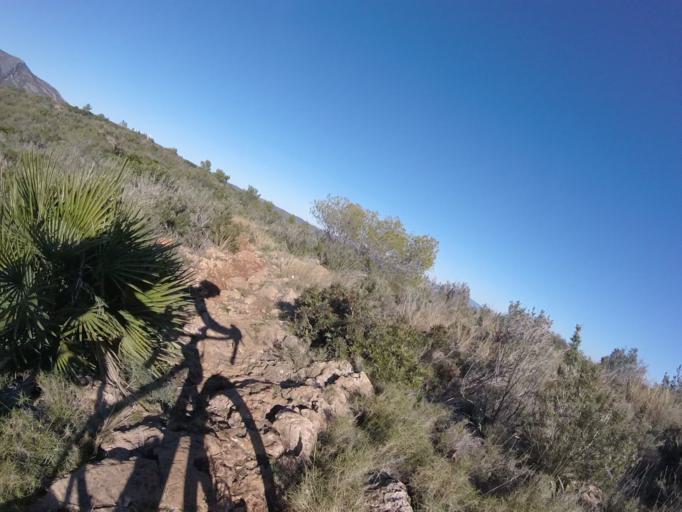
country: ES
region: Valencia
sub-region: Provincia de Castello
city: Orpesa/Oropesa del Mar
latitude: 40.1106
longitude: 0.1204
